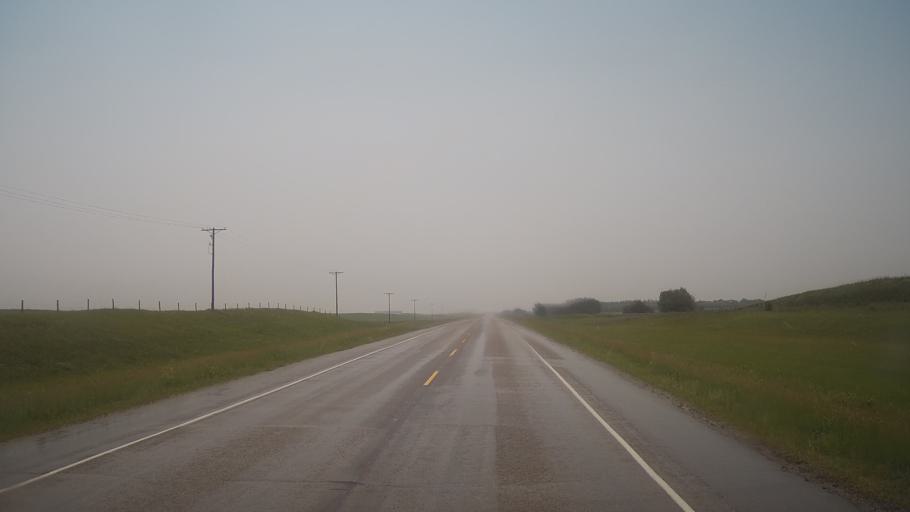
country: CA
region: Saskatchewan
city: Biggar
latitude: 52.0838
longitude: -108.0380
